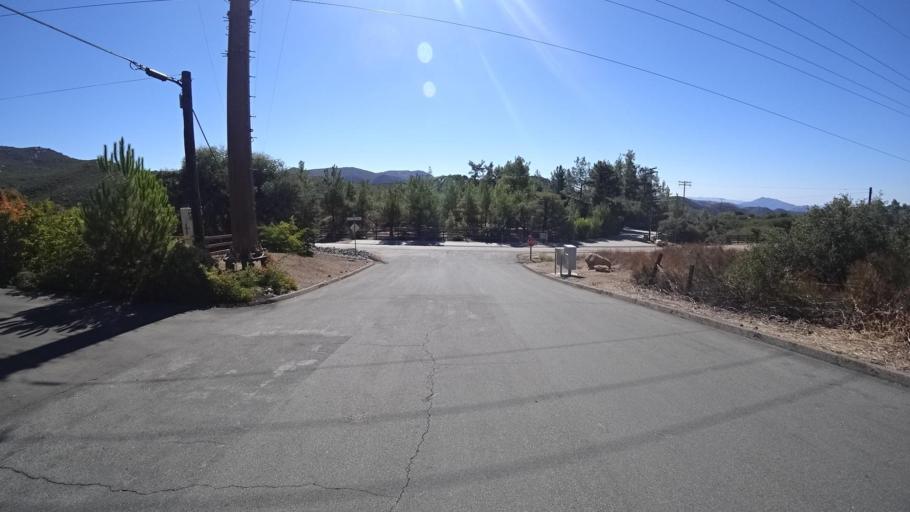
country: US
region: California
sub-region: San Diego County
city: Descanso
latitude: 32.8068
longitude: -116.6391
